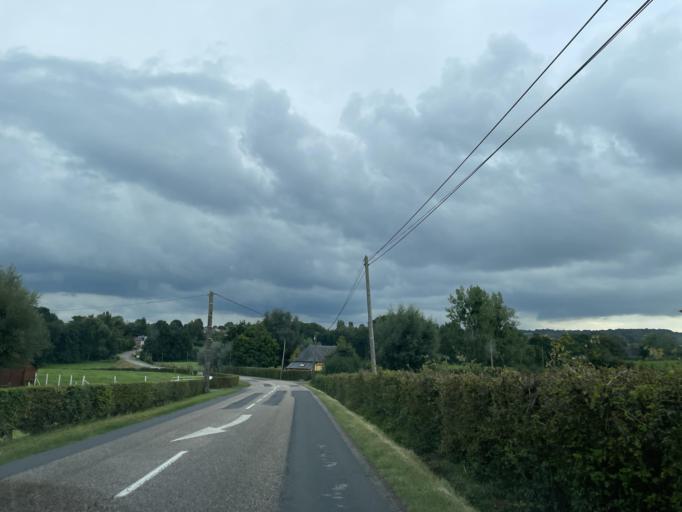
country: FR
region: Haute-Normandie
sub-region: Departement de la Seine-Maritime
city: Neufchatel-en-Bray
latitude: 49.6819
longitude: 1.4296
